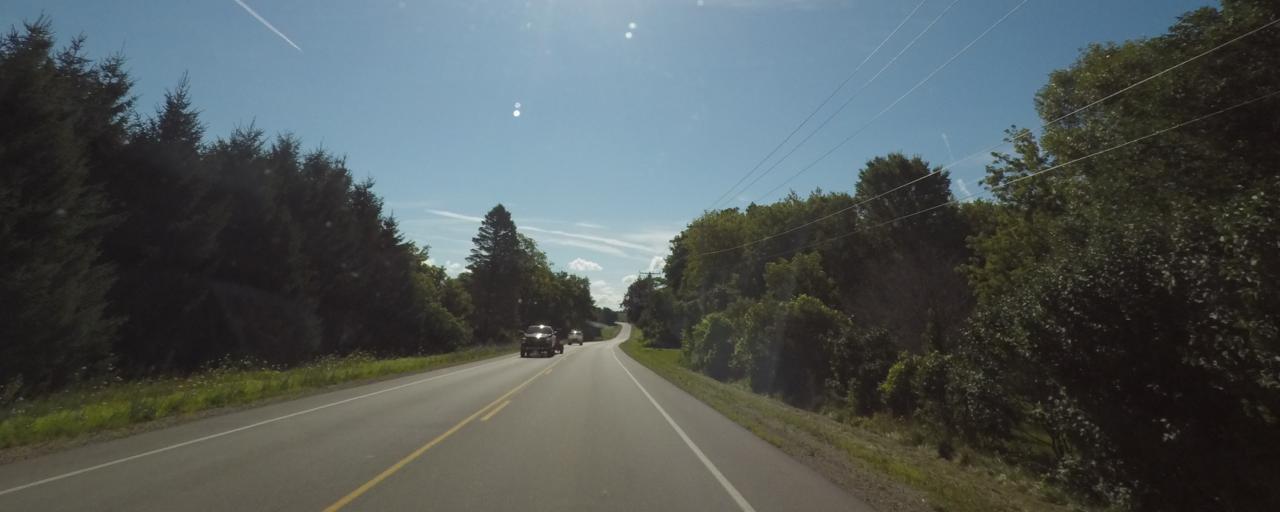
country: US
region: Wisconsin
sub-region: Jefferson County
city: Johnson Creek
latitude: 43.0733
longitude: -88.7075
